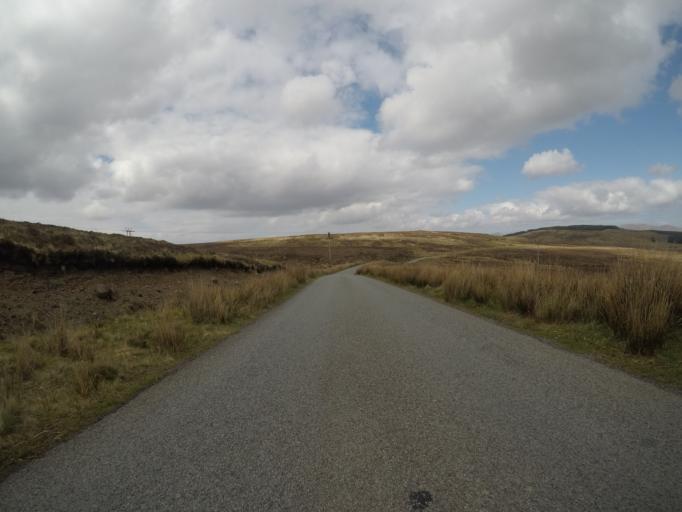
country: GB
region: Scotland
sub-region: Highland
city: Isle of Skye
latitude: 57.3997
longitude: -6.3374
